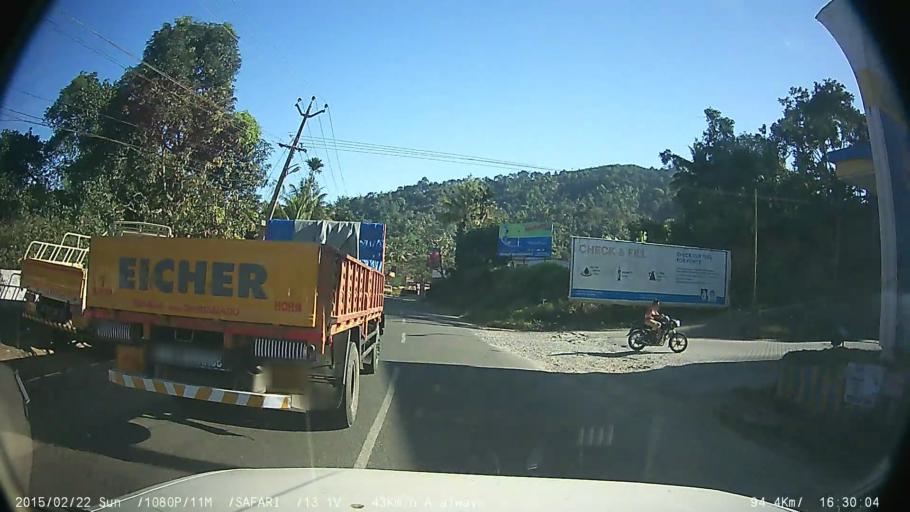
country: IN
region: Tamil Nadu
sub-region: Theni
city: Gudalur
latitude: 9.6132
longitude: 77.1568
